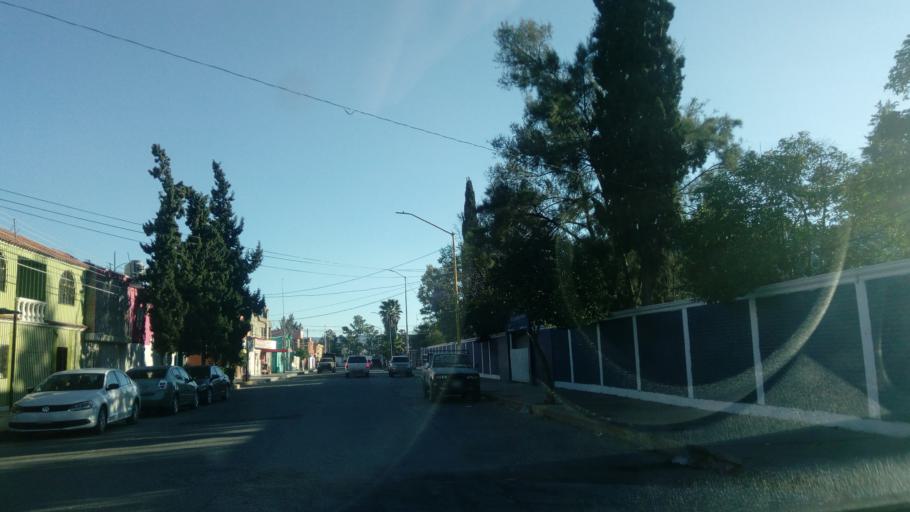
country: MX
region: Durango
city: Victoria de Durango
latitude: 23.9997
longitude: -104.6777
